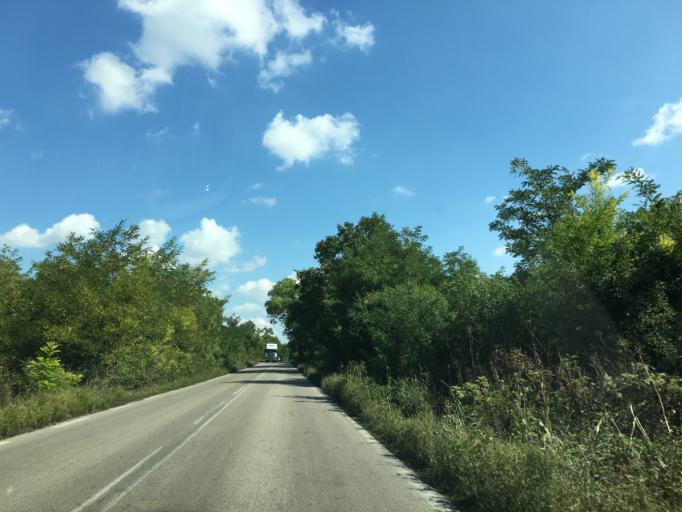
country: BG
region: Montana
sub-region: Obshtina Lom
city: Lom
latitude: 43.8000
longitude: 23.1460
